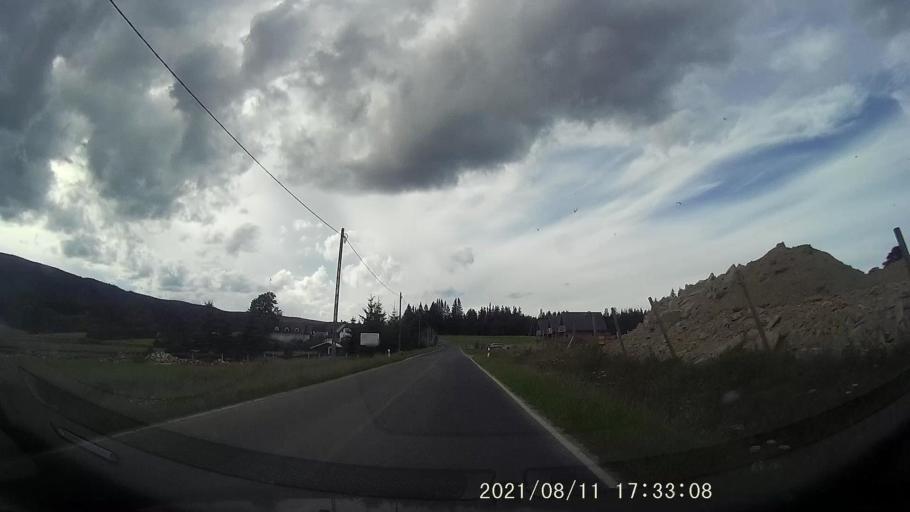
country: PL
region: Lower Silesian Voivodeship
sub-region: Powiat klodzki
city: Szczytna
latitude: 50.3144
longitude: 16.4458
